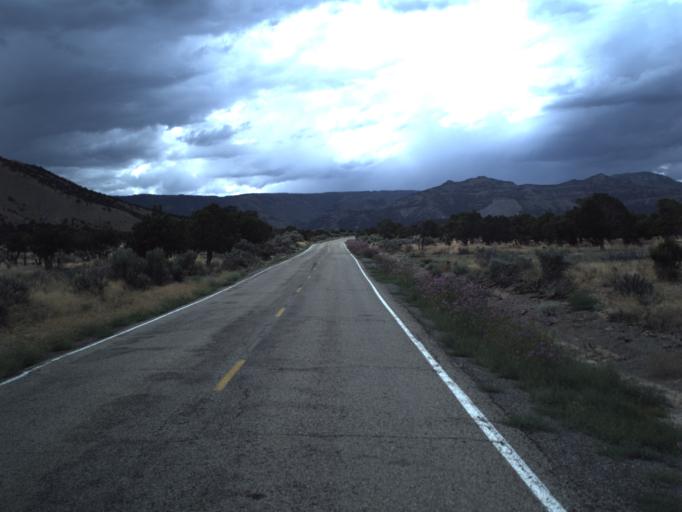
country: US
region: Utah
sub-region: Emery County
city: Huntington
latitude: 39.4844
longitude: -110.9256
